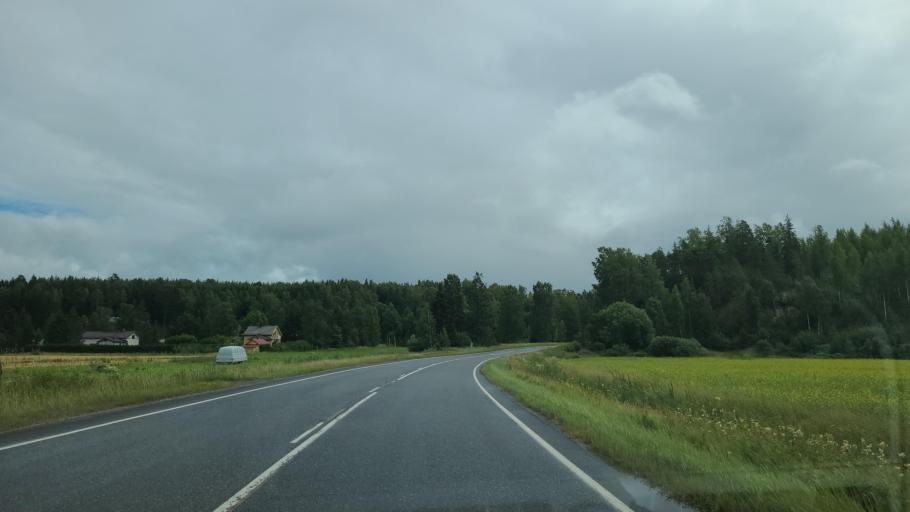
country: FI
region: Varsinais-Suomi
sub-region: Turku
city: Sauvo
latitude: 60.3401
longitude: 22.6972
